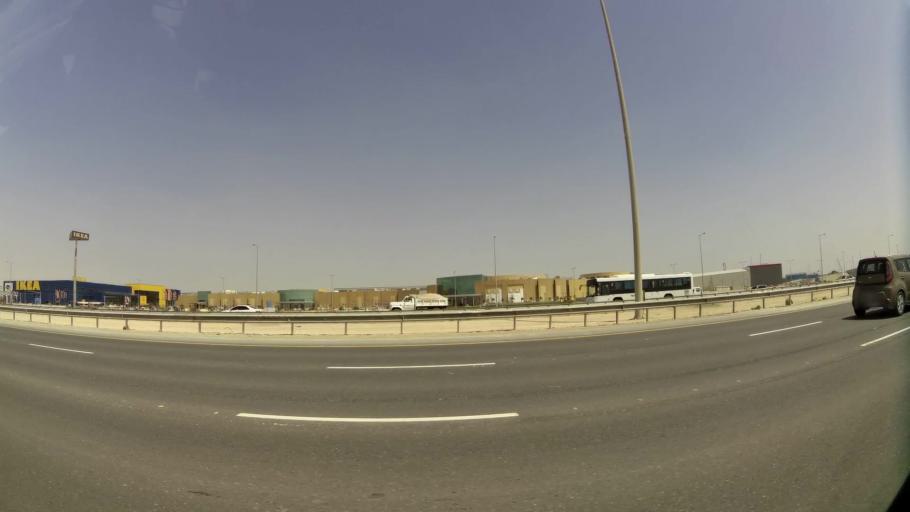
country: QA
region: Baladiyat Umm Salal
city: Umm Salal Muhammad
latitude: 25.3837
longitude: 51.4381
